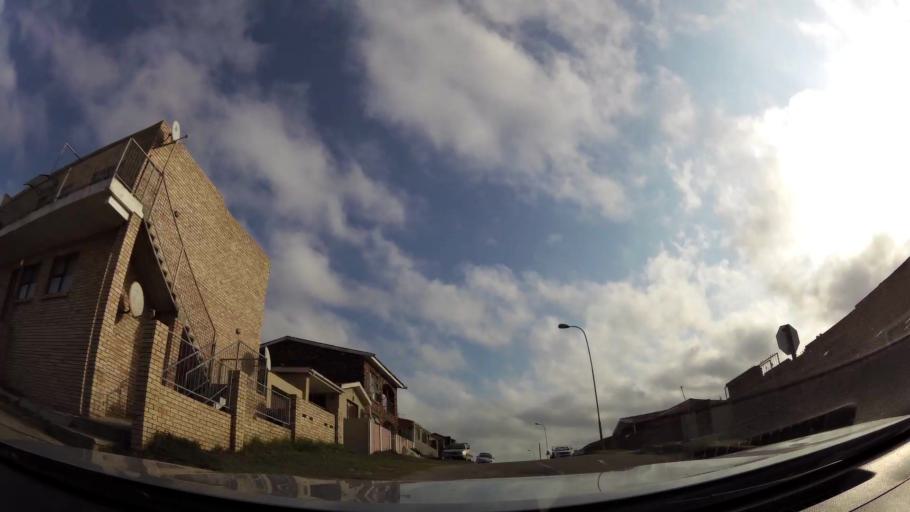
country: ZA
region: Eastern Cape
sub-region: Nelson Mandela Bay Metropolitan Municipality
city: Port Elizabeth
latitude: -33.9224
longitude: 25.5513
